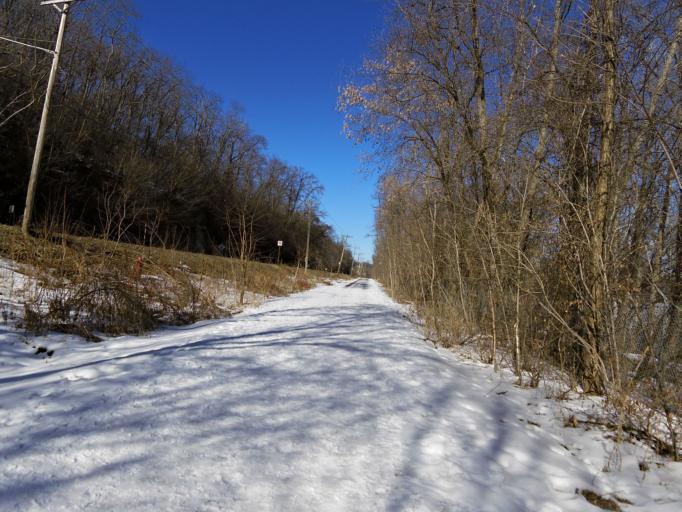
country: US
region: Minnesota
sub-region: Washington County
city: Stillwater
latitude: 45.0661
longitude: -92.8059
